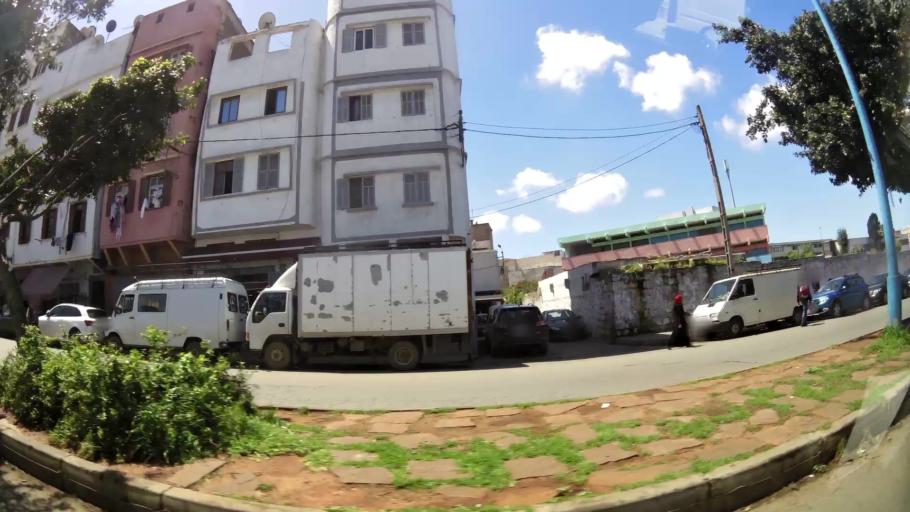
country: MA
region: Grand Casablanca
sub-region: Casablanca
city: Casablanca
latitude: 33.5667
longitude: -7.5992
